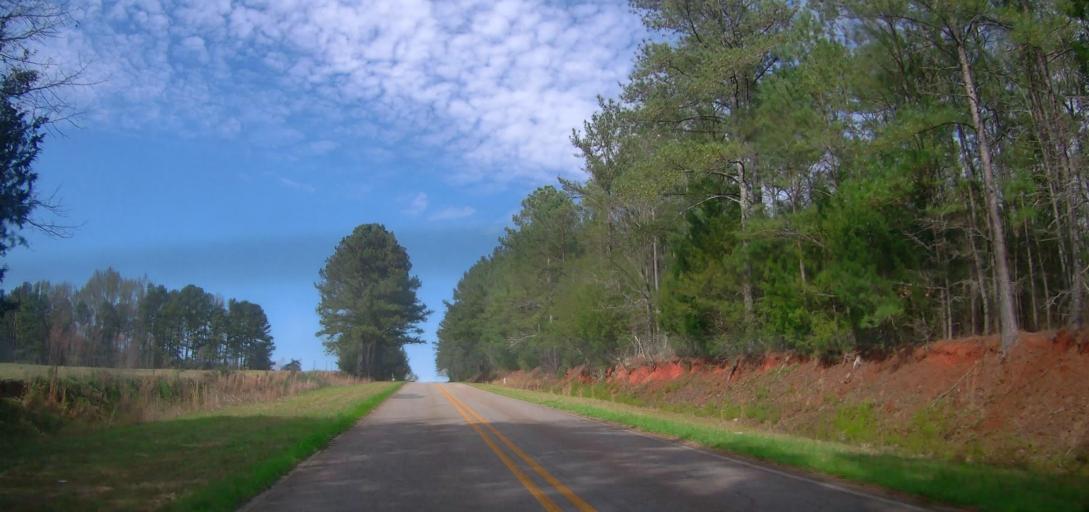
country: US
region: Georgia
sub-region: Monroe County
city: Forsyth
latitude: 33.0205
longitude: -83.8784
